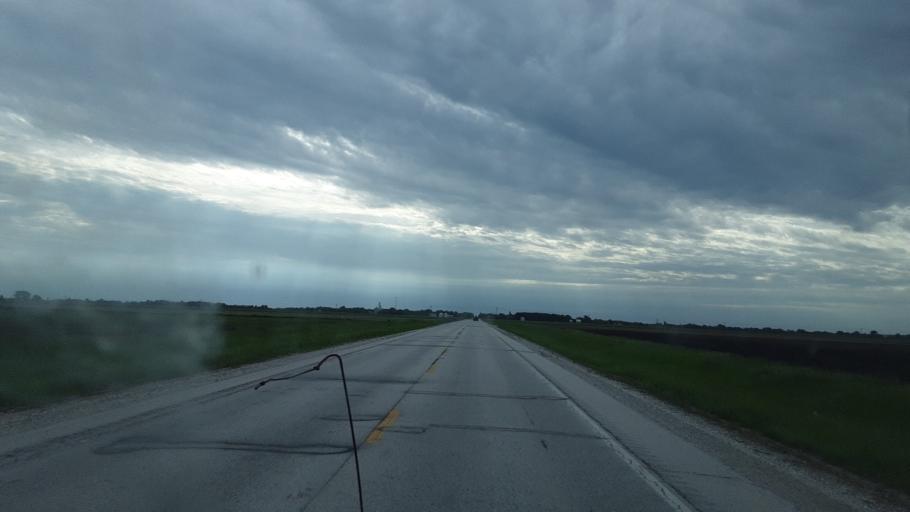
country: US
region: Illinois
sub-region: Hancock County
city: Hamilton
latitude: 40.3955
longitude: -91.2794
